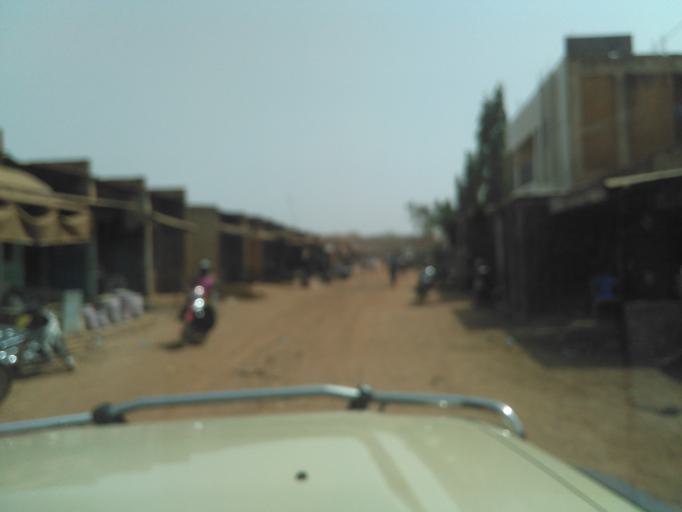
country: BF
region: Centre
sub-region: Kadiogo Province
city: Ouagadougou
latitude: 12.3889
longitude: -1.5653
